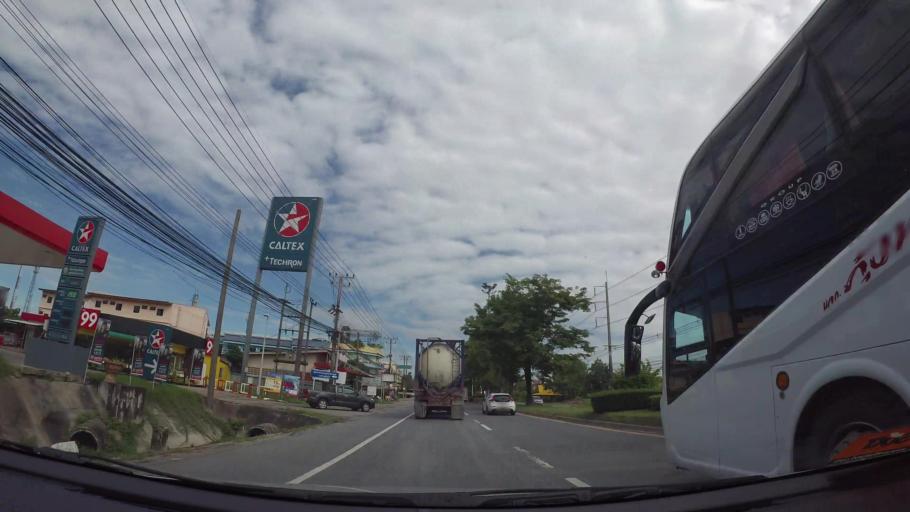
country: TH
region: Rayong
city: Ban Chang
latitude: 12.7352
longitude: 101.1309
